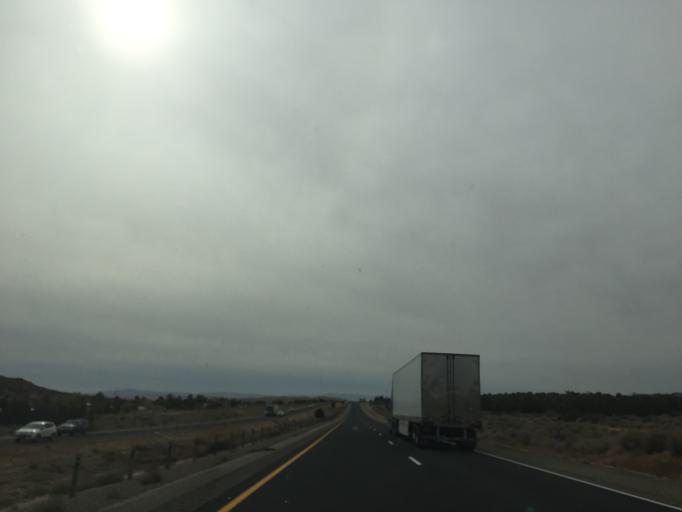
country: US
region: Utah
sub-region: Washington County
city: Toquerville
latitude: 37.2656
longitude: -113.3244
